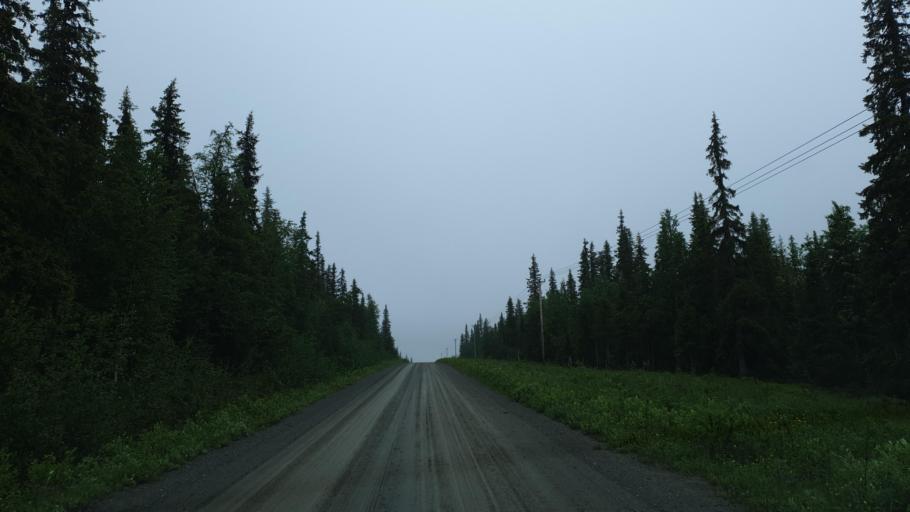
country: SE
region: Vaesterbotten
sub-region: Vilhelmina Kommun
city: Sjoberg
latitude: 65.3179
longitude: 15.9485
